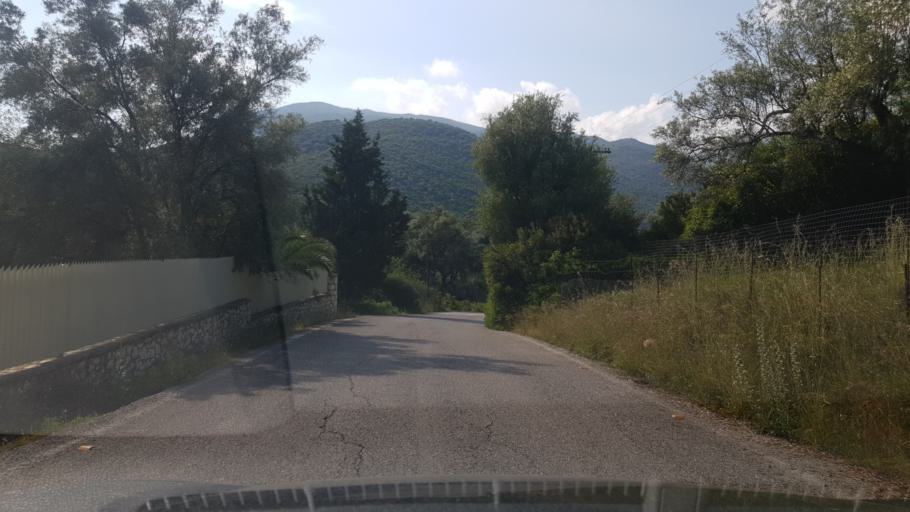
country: GR
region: Ionian Islands
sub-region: Lefkada
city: Nidri
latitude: 38.6547
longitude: 20.7022
